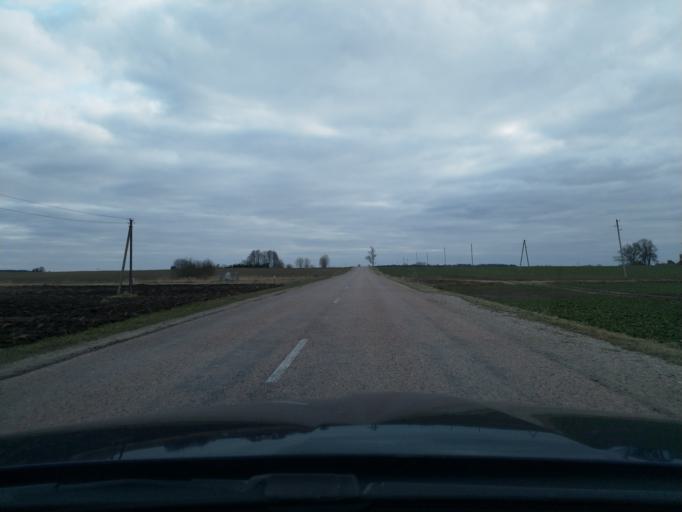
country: LV
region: Talsu Rajons
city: Sabile
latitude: 56.9548
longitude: 22.6101
